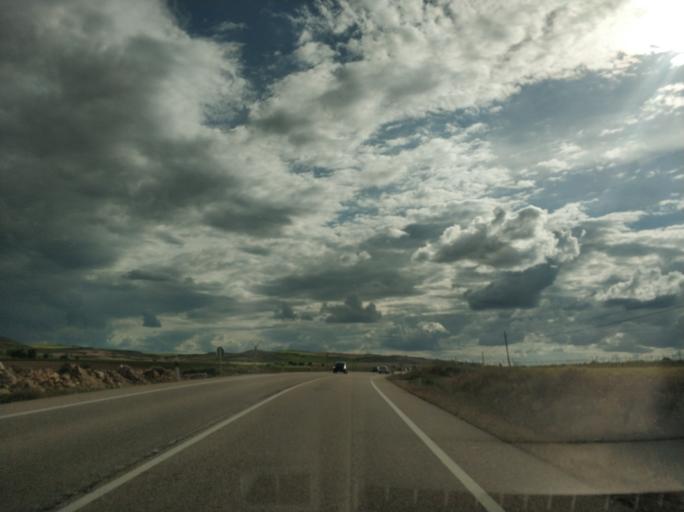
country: ES
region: Castille and Leon
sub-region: Provincia de Burgos
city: Castrillo de la Vega
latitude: 41.6429
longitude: -3.7927
